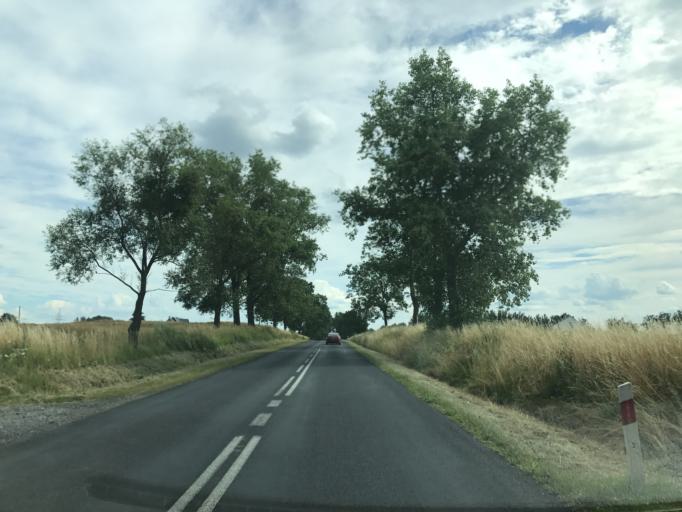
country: PL
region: Kujawsko-Pomorskie
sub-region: Powiat rypinski
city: Rypin
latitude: 53.0468
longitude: 19.3677
